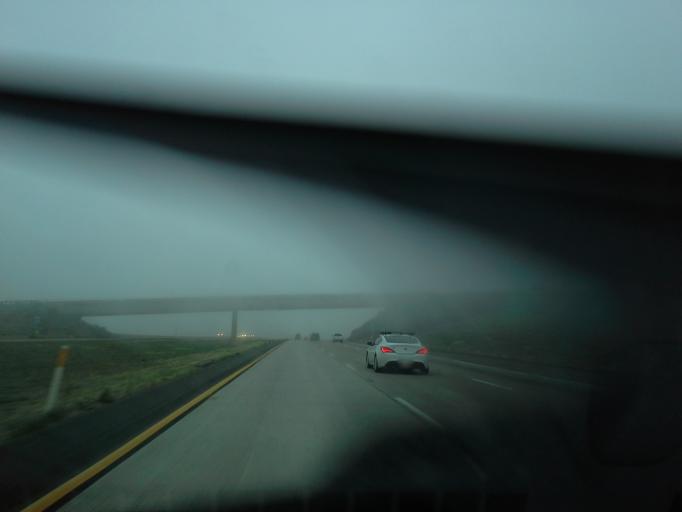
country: US
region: California
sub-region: San Diego County
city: Descanso
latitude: 32.8379
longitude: -116.6834
